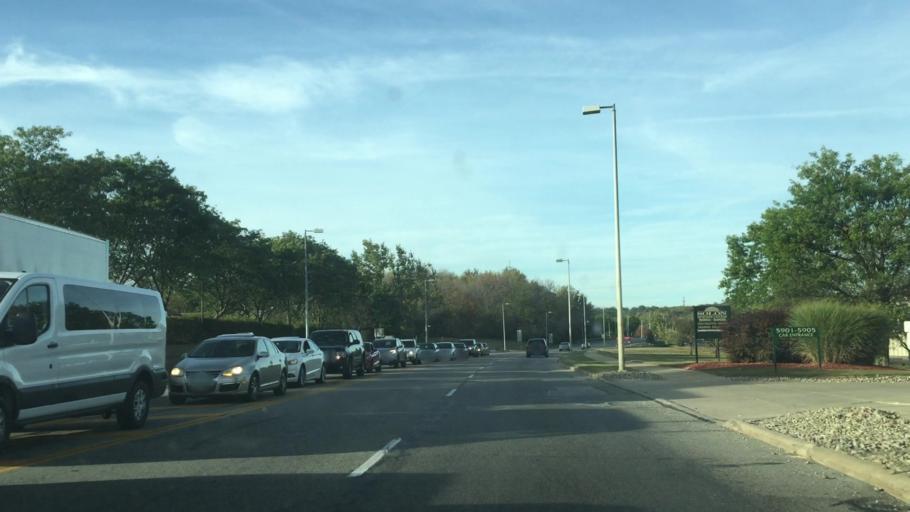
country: US
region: Ohio
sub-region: Cuyahoga County
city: Solon
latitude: 41.3990
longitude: -81.4688
